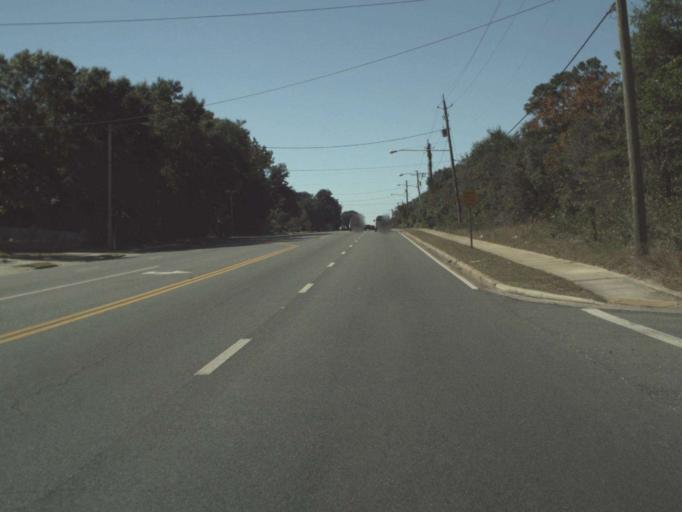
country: US
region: Florida
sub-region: Okaloosa County
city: Ocean City
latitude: 30.4272
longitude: -86.6235
